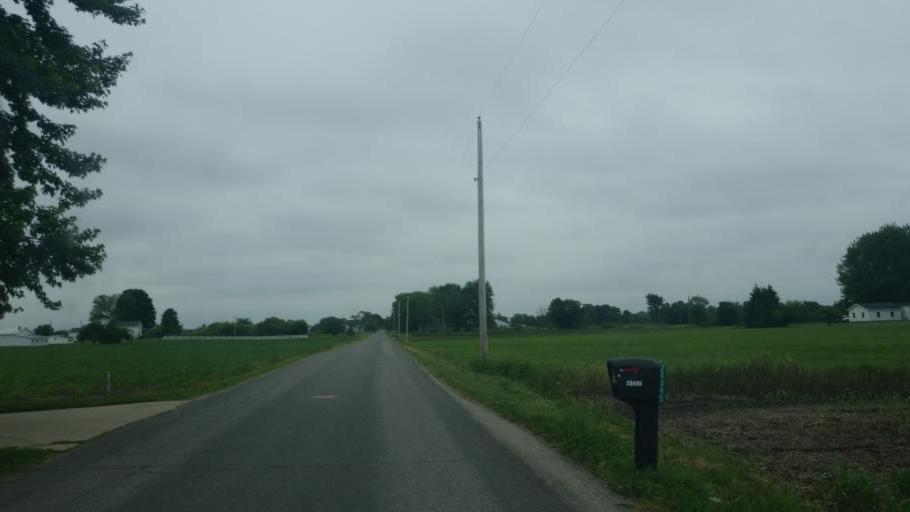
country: US
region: Indiana
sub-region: Elkhart County
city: Nappanee
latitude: 41.4716
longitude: -86.0306
